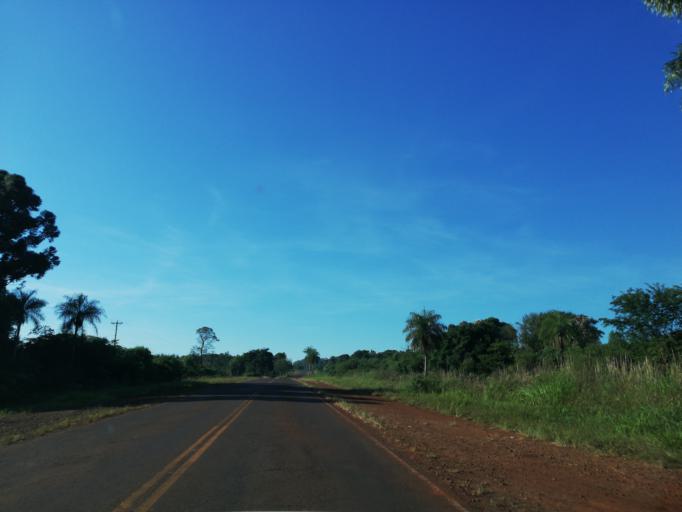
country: AR
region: Misiones
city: Gobernador Roca
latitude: -27.1873
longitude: -55.4467
